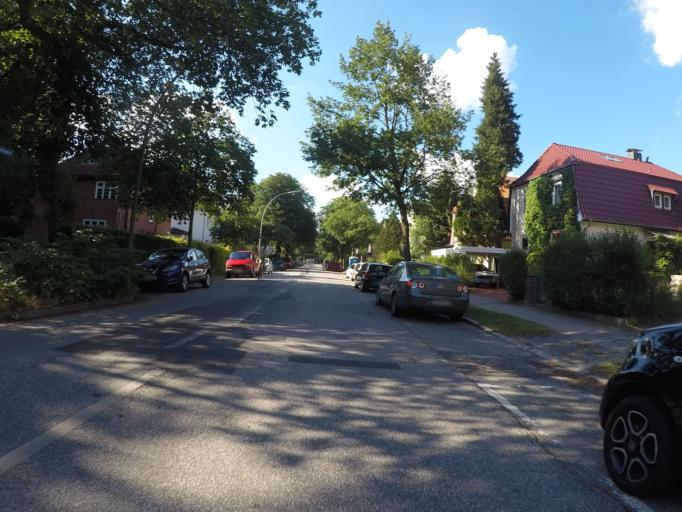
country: DE
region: Hamburg
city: Ohlsdorf
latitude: 53.6337
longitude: 10.0257
